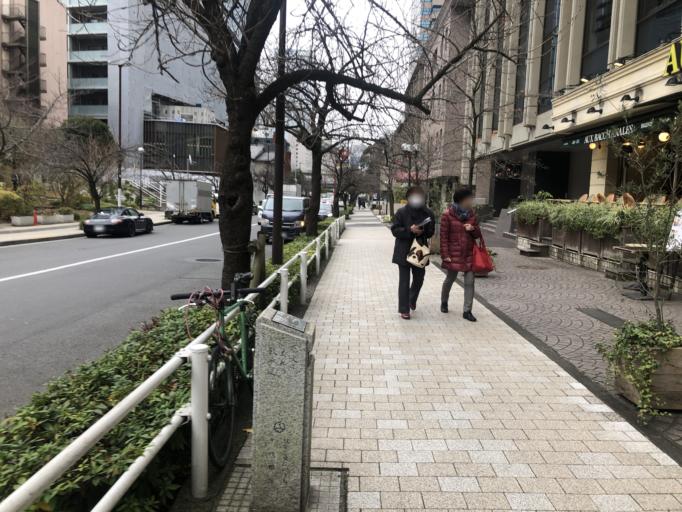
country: JP
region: Tokyo
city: Tokyo
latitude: 35.6812
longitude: 139.7353
